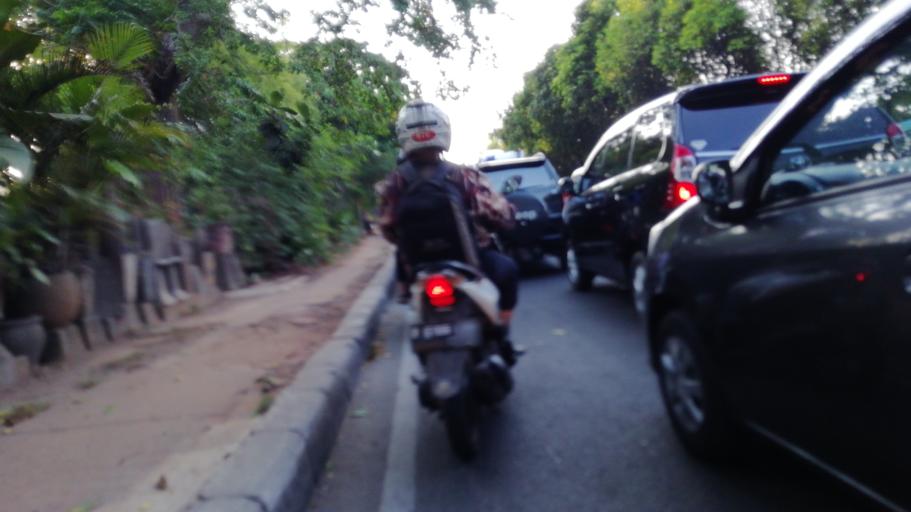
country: ID
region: Jakarta Raya
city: Jakarta
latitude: -6.2947
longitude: 106.8237
